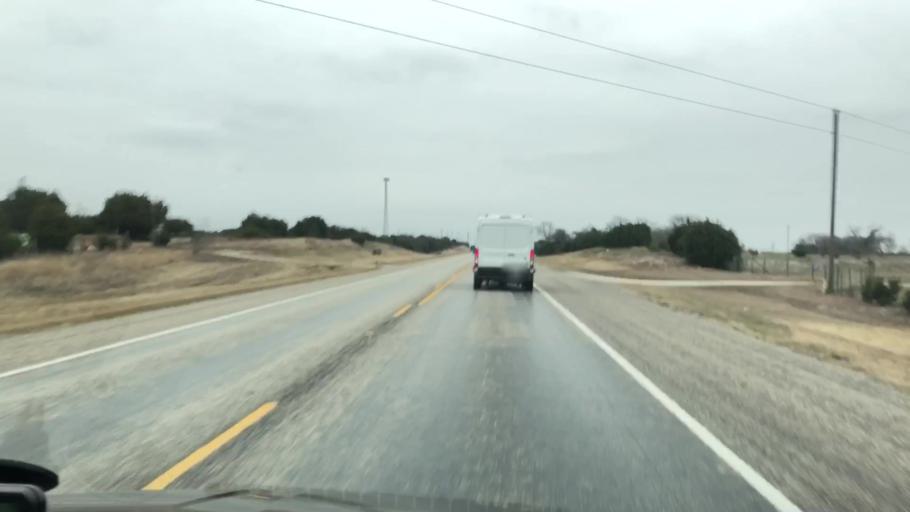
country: US
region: Texas
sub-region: Lampasas County
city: Lampasas
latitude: 31.1275
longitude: -98.1893
